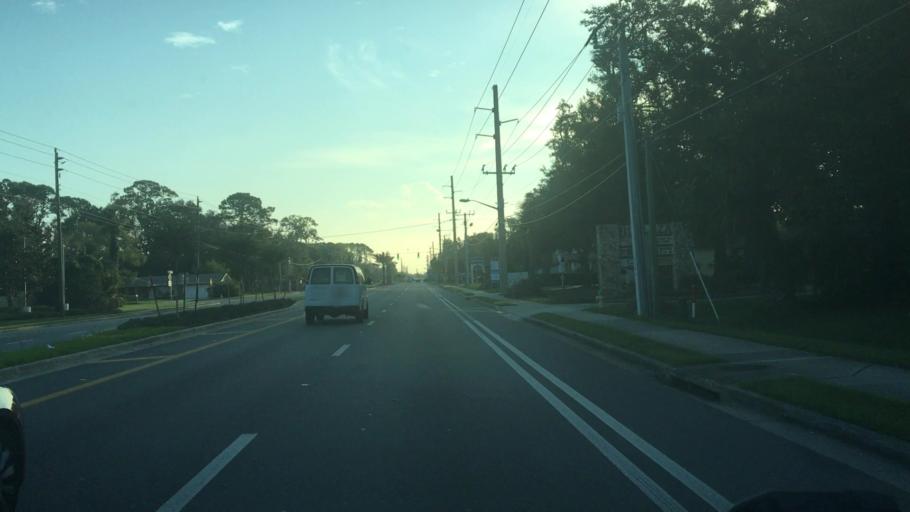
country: US
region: Florida
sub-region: Volusia County
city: South Daytona
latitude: 29.1767
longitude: -81.0249
